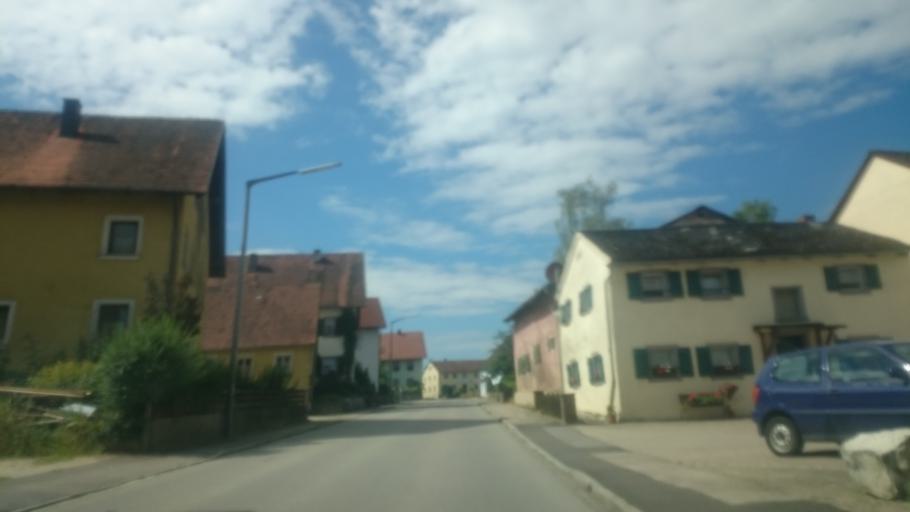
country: DE
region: Bavaria
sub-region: Regierungsbezirk Mittelfranken
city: Ettenstatt
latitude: 49.0298
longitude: 11.0478
